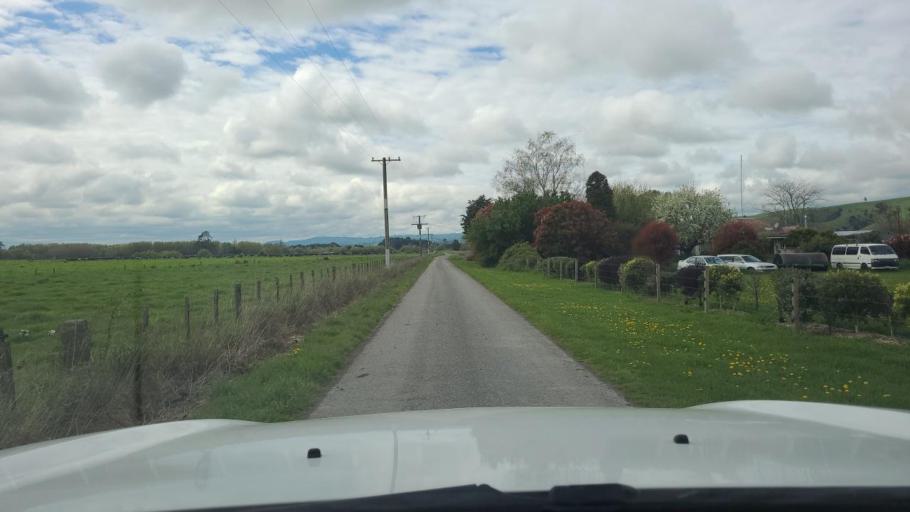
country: NZ
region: Wellington
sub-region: Masterton District
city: Masterton
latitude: -41.0958
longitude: 175.4934
